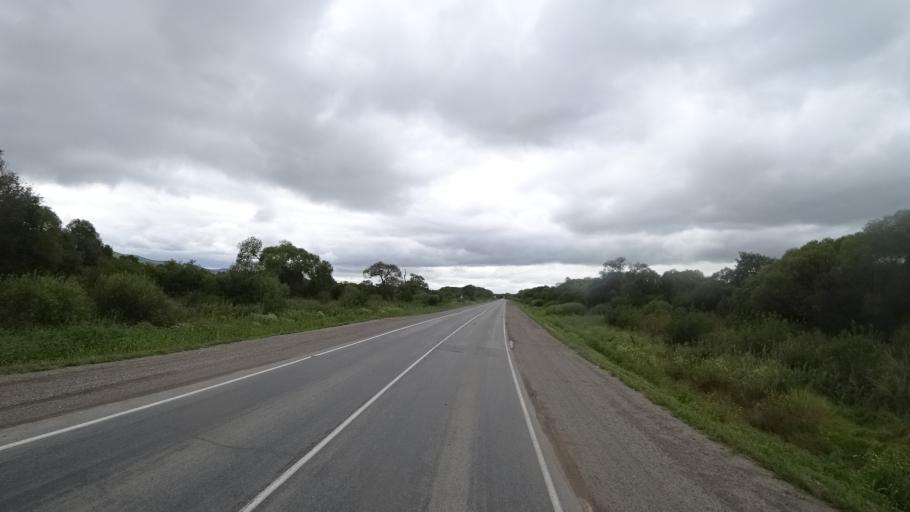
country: RU
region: Primorskiy
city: Chernigovka
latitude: 44.3456
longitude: 132.6054
